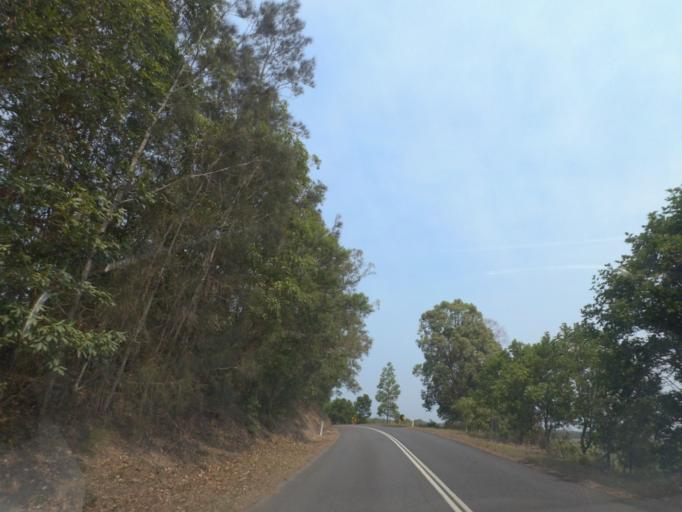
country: AU
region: New South Wales
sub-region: Tweed
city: Burringbar
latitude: -28.4542
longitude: 153.5351
